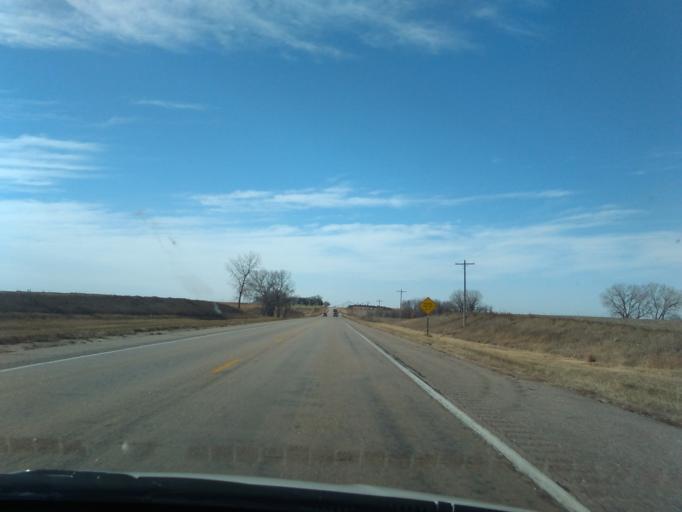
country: US
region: Nebraska
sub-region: Clay County
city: Harvard
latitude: 40.5827
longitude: -98.0611
